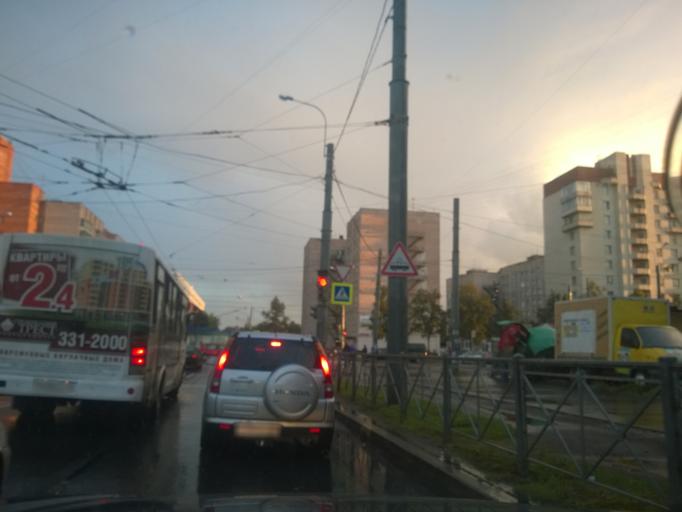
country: RU
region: St.-Petersburg
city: Uritsk
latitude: 59.8335
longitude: 30.1822
